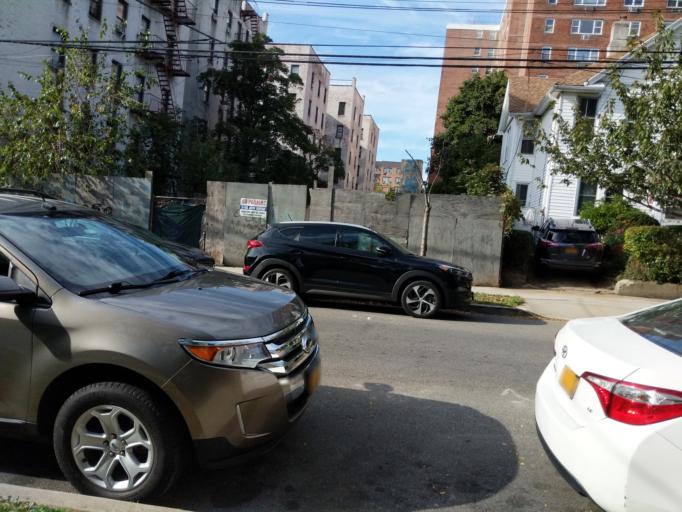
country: US
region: New York
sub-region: Queens County
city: Jamaica
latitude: 40.7087
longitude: -73.7911
